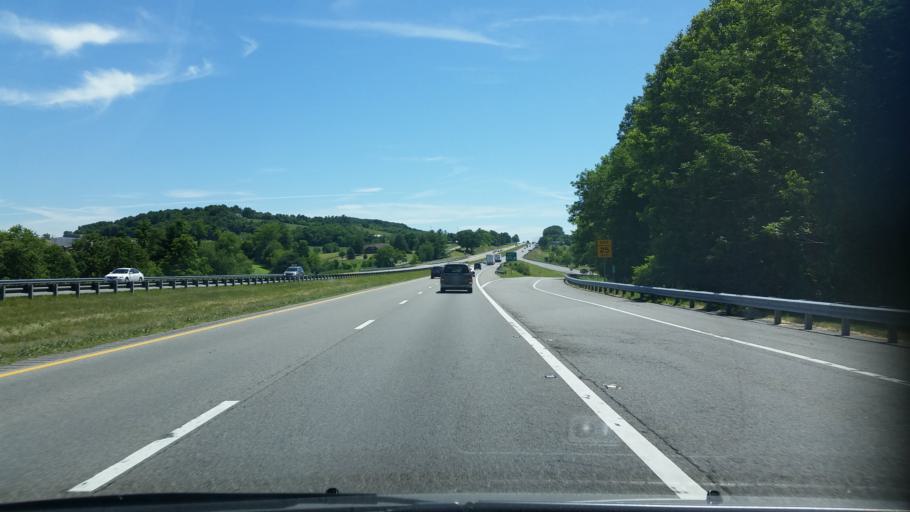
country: US
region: Virginia
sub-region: Wythe County
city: Rural Retreat
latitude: 36.9153
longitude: -81.2768
